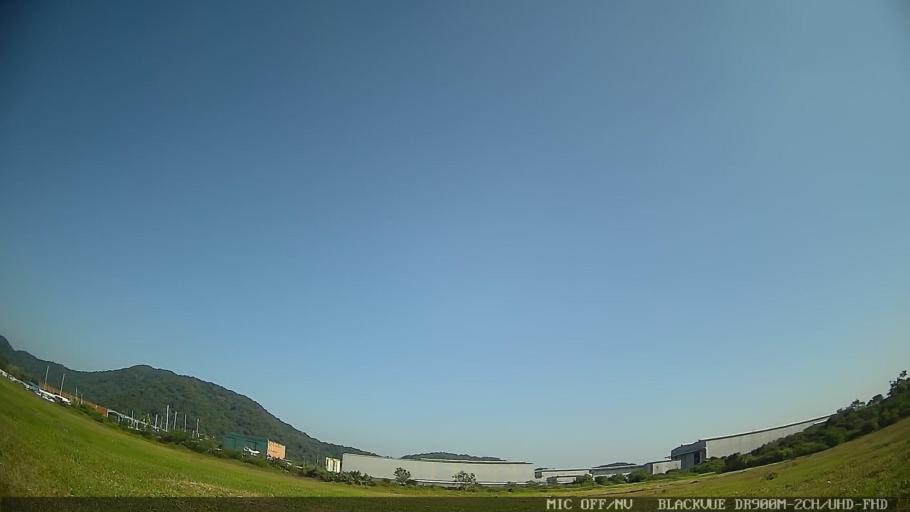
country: BR
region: Sao Paulo
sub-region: Guaruja
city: Guaruja
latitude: -24.0033
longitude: -46.2948
